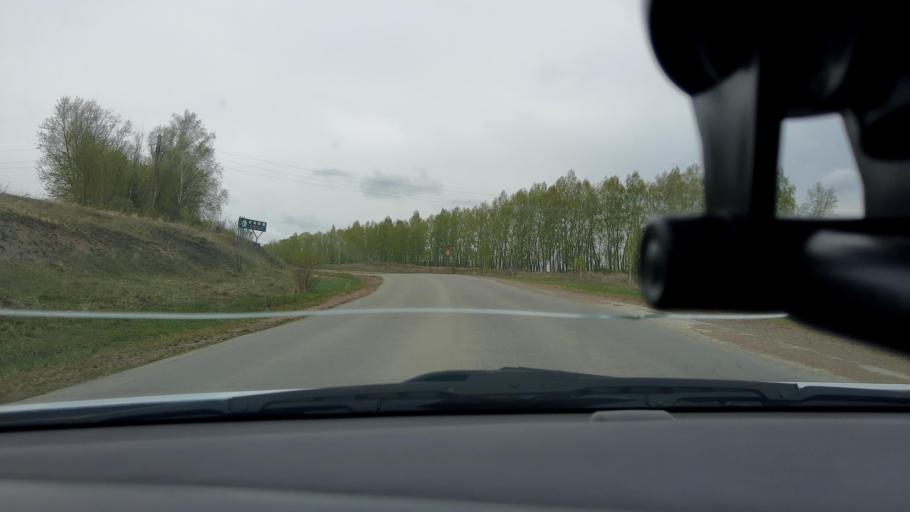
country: RU
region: Bashkortostan
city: Yazykovo
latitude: 55.1356
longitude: 56.0858
